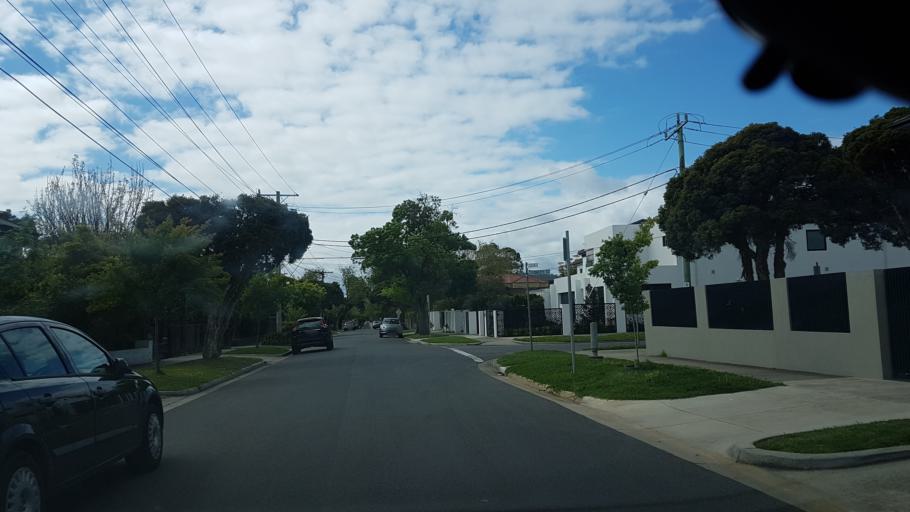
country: AU
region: Victoria
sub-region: Bayside
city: Hampton East
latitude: -37.9272
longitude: 145.0193
